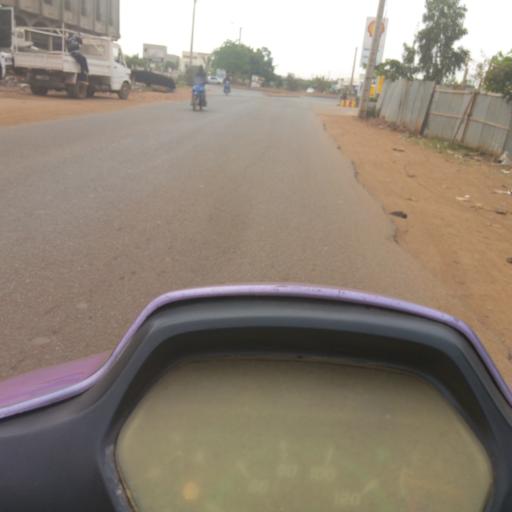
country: ML
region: Bamako
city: Bamako
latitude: 12.6543
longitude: -7.9363
